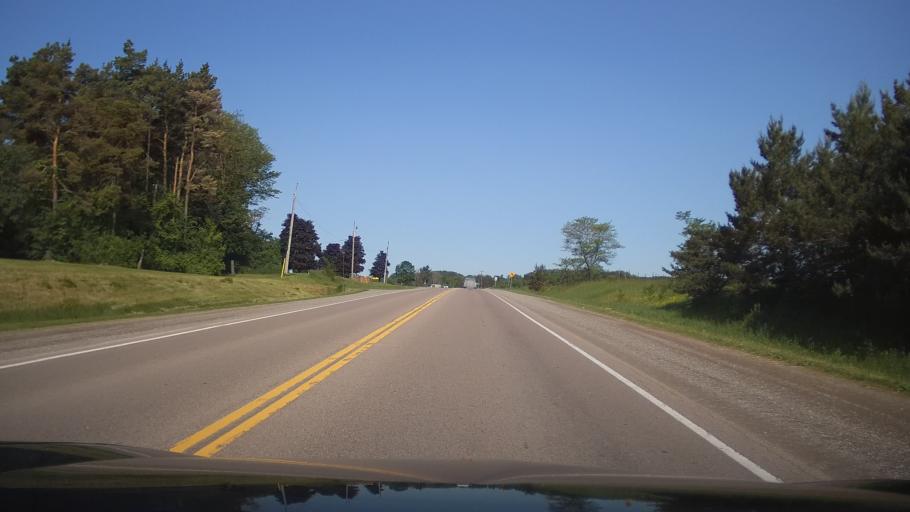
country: CA
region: Ontario
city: Omemee
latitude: 44.3476
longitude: -78.7812
